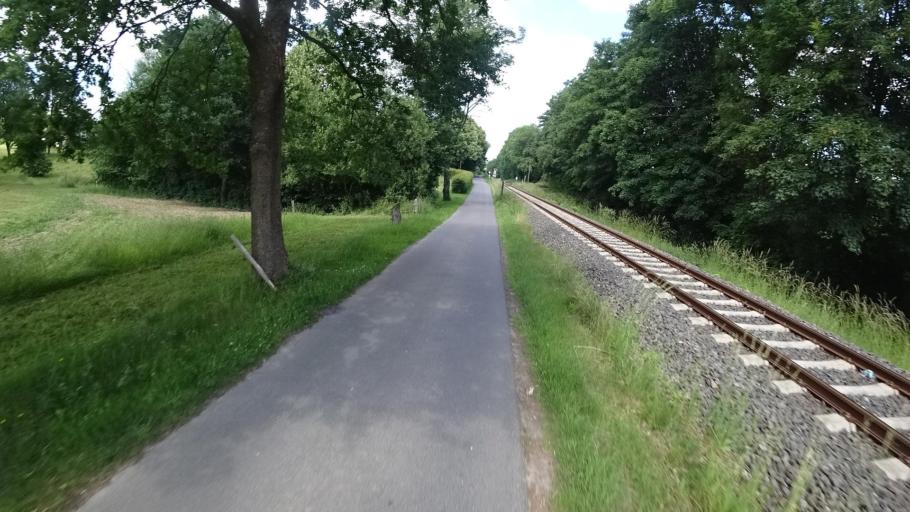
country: DE
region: Rheinland-Pfalz
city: Bachenberg
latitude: 50.7103
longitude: 7.6575
